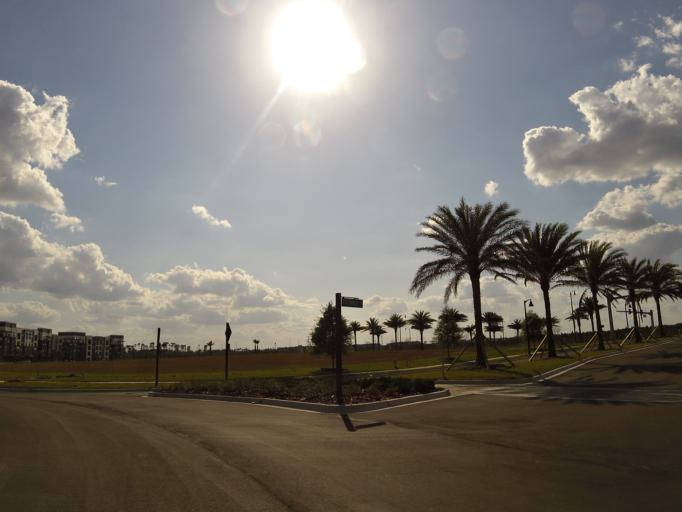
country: US
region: Florida
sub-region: Saint Johns County
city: Palm Valley
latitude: 30.1672
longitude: -81.5058
